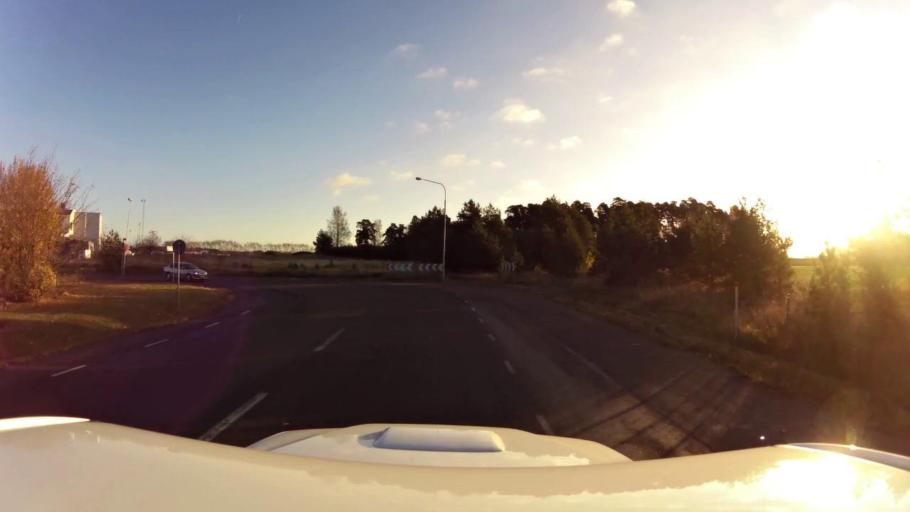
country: SE
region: OEstergoetland
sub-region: Linkopings Kommun
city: Linkoping
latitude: 58.4188
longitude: 15.6798
